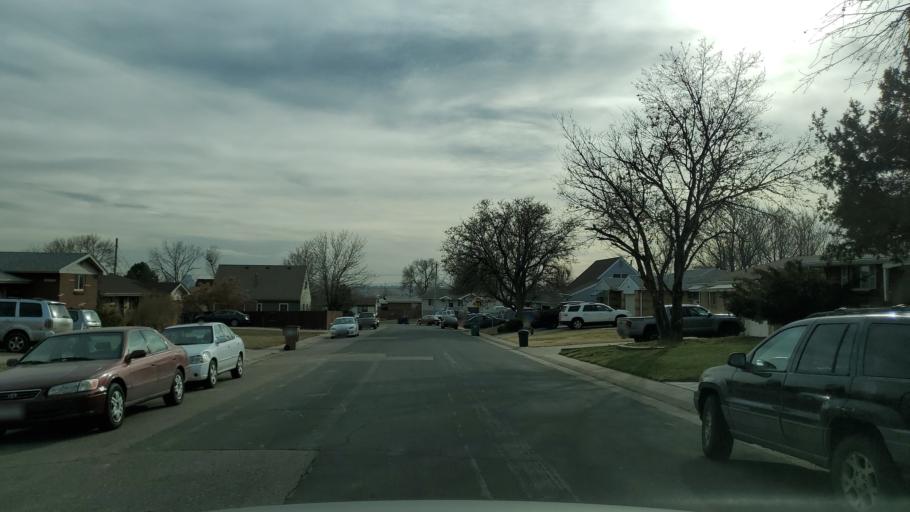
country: US
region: Colorado
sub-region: Adams County
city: Westminster
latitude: 39.8298
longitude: -105.0234
